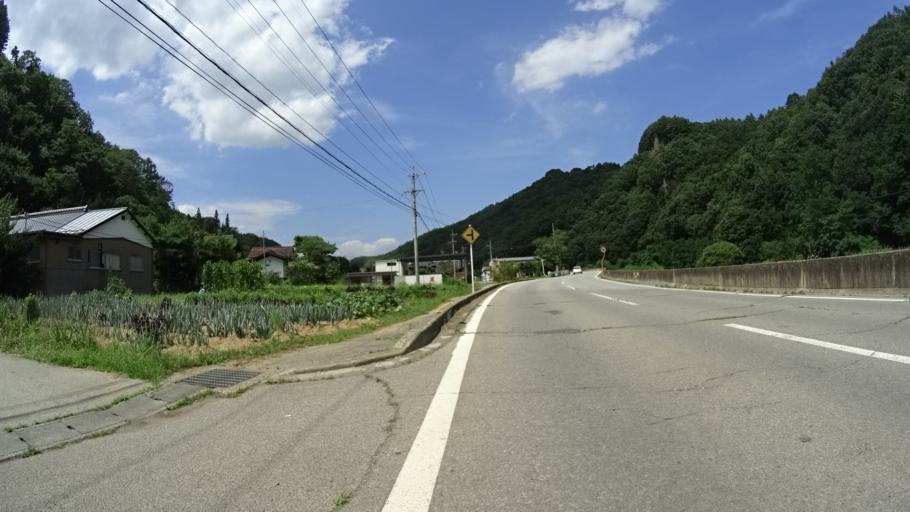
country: JP
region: Nagano
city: Saku
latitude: 36.0700
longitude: 138.4972
